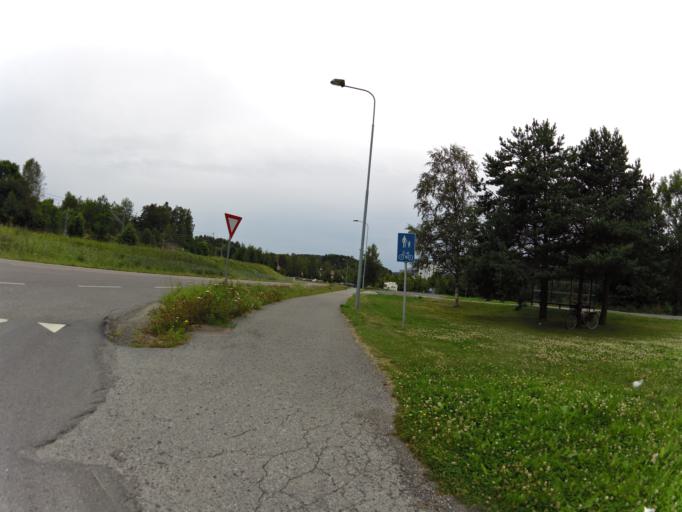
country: NO
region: Ostfold
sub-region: Moss
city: Moss
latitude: 59.4800
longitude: 10.6933
